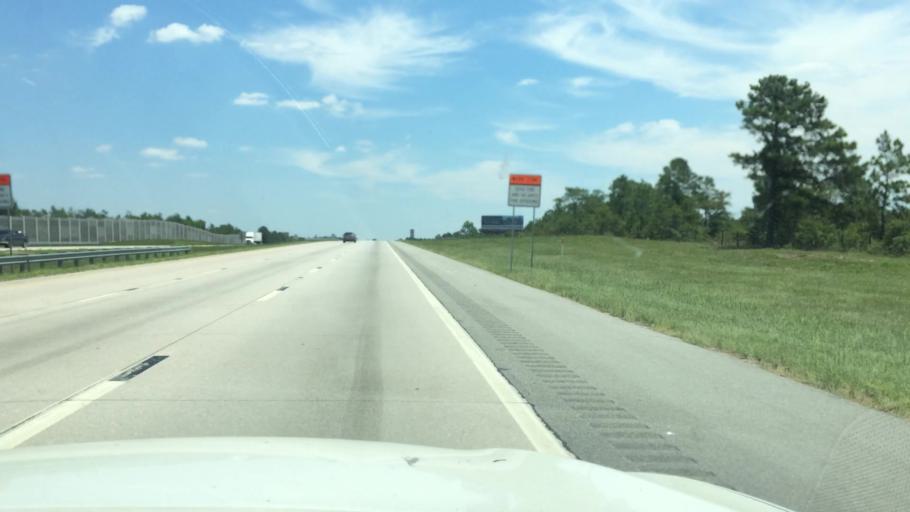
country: US
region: South Carolina
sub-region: Kershaw County
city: Elgin
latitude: 34.0983
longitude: -80.8467
